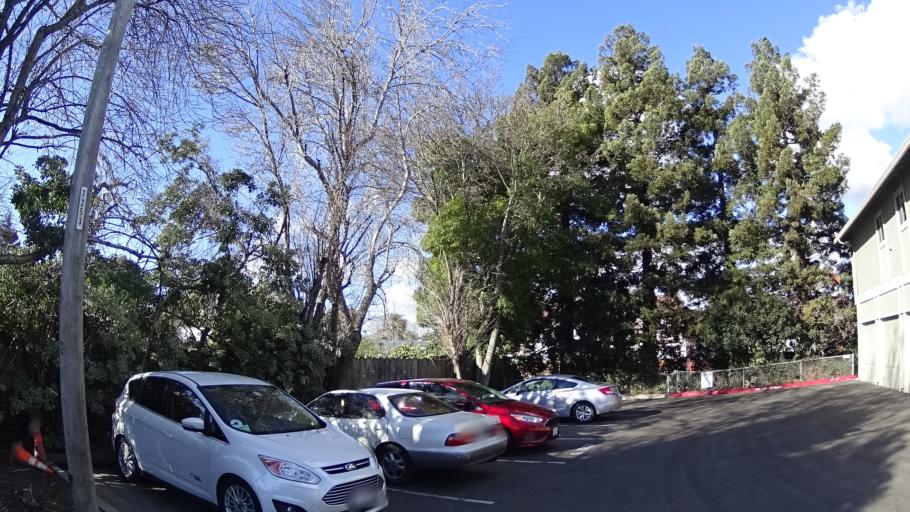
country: US
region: California
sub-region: Alameda County
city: San Lorenzo
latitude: 37.6855
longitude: -122.1194
